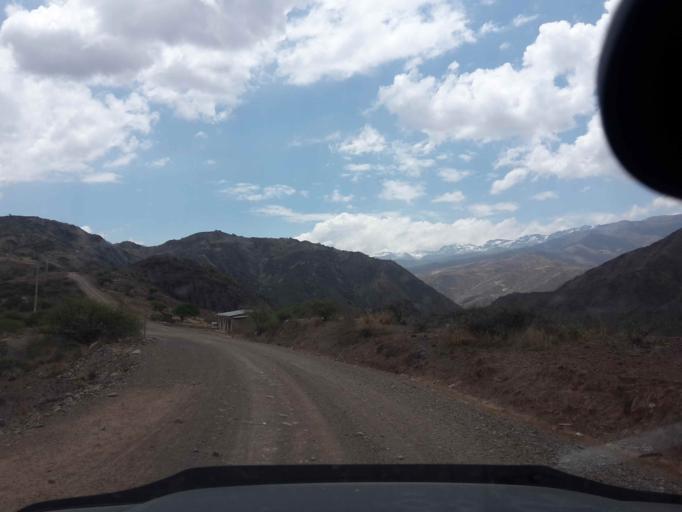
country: BO
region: Cochabamba
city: Sipe Sipe
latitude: -17.5353
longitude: -66.4896
